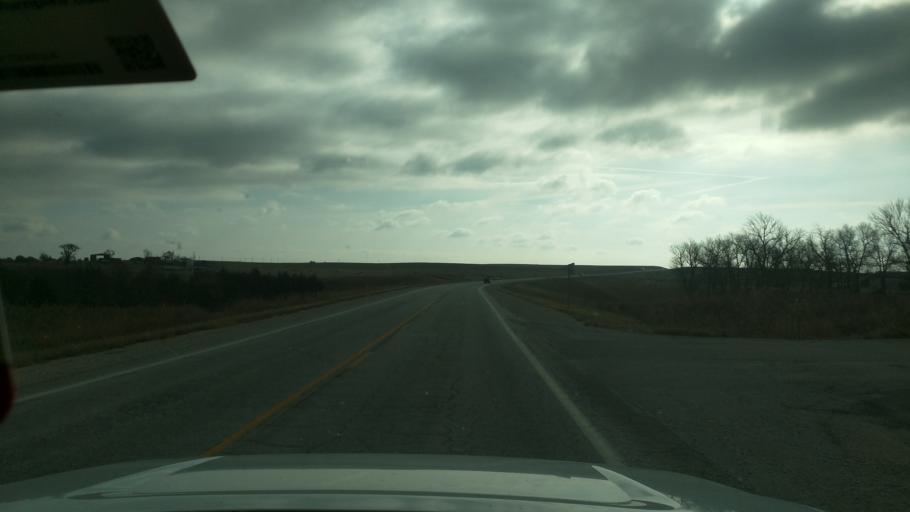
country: US
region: Kansas
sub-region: Chautauqua County
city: Sedan
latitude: 37.1029
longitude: -96.2396
